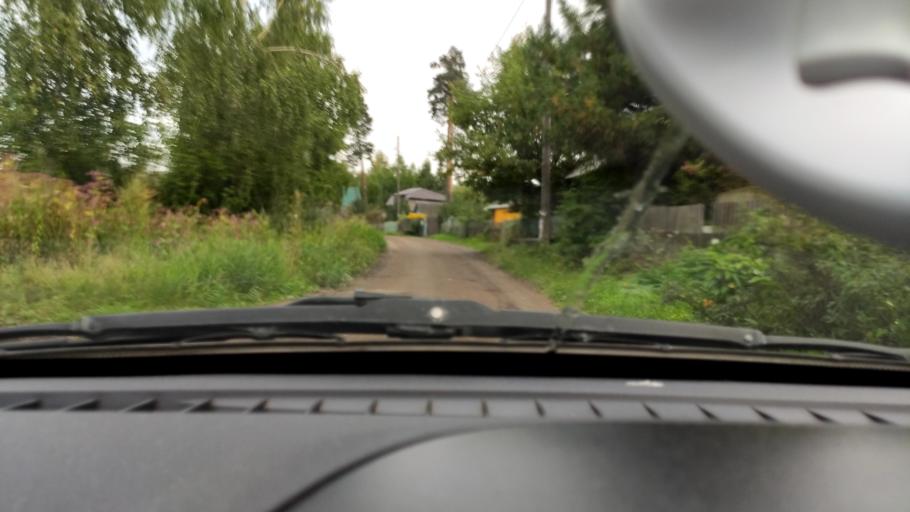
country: RU
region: Perm
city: Overyata
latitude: 58.0190
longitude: 55.9634
